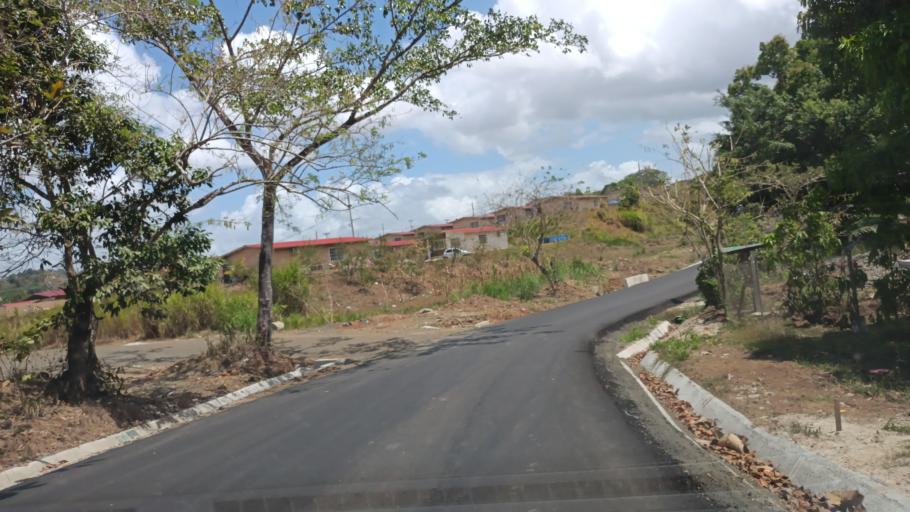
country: PA
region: Panama
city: Alcalde Diaz
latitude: 9.0977
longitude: -79.5739
